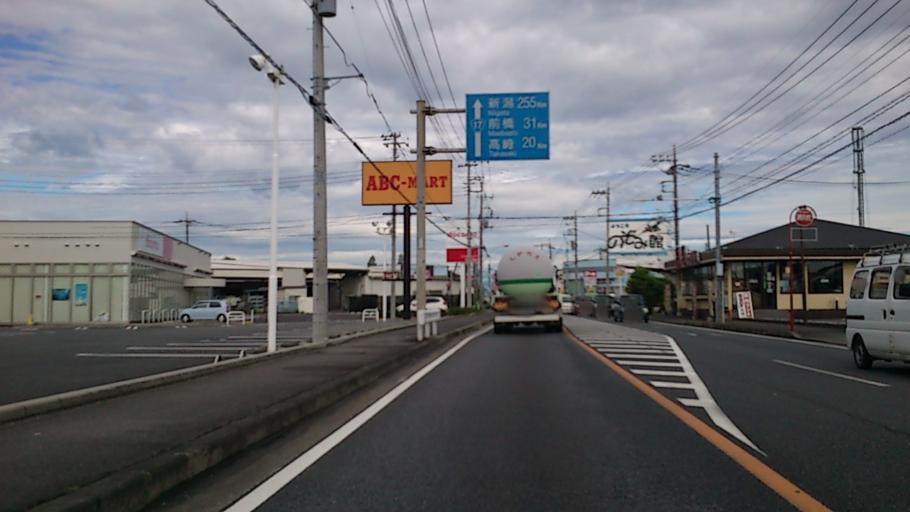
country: JP
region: Saitama
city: Honjo
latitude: 36.2495
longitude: 139.1811
